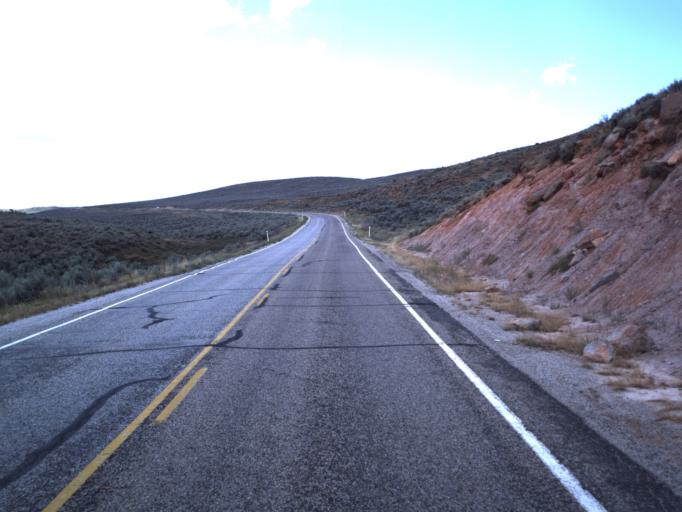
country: US
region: Utah
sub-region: Rich County
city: Randolph
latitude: 41.7893
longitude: -111.2127
